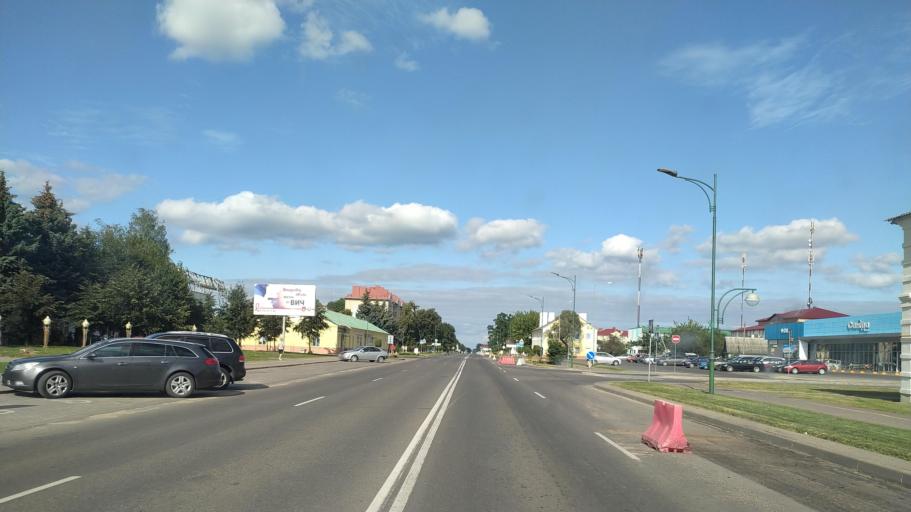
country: BY
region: Brest
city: Byaroza
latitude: 52.5286
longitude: 24.9730
